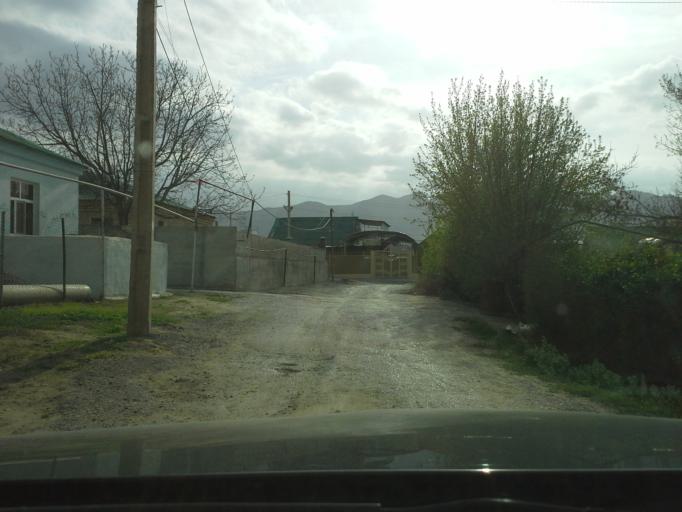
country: TM
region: Ahal
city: Abadan
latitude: 37.9625
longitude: 58.2288
